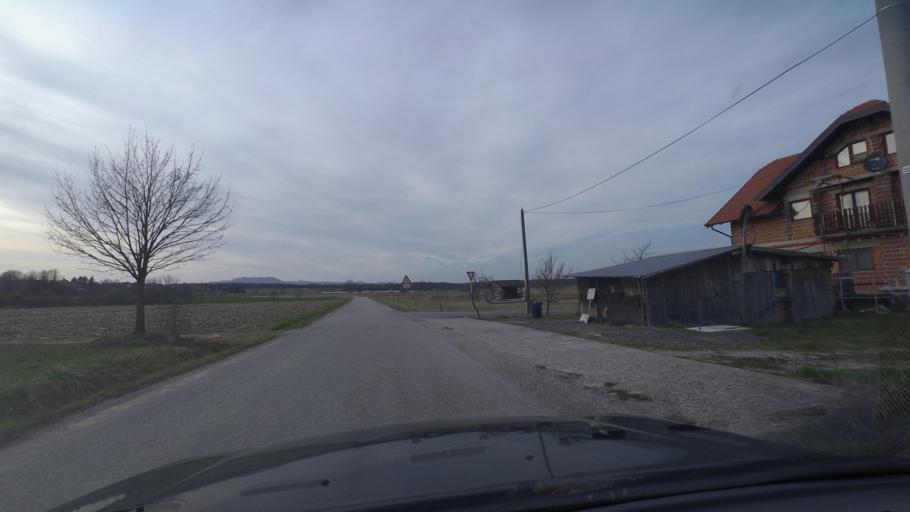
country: HR
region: Grad Zagreb
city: Horvati
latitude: 45.6896
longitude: 15.8498
